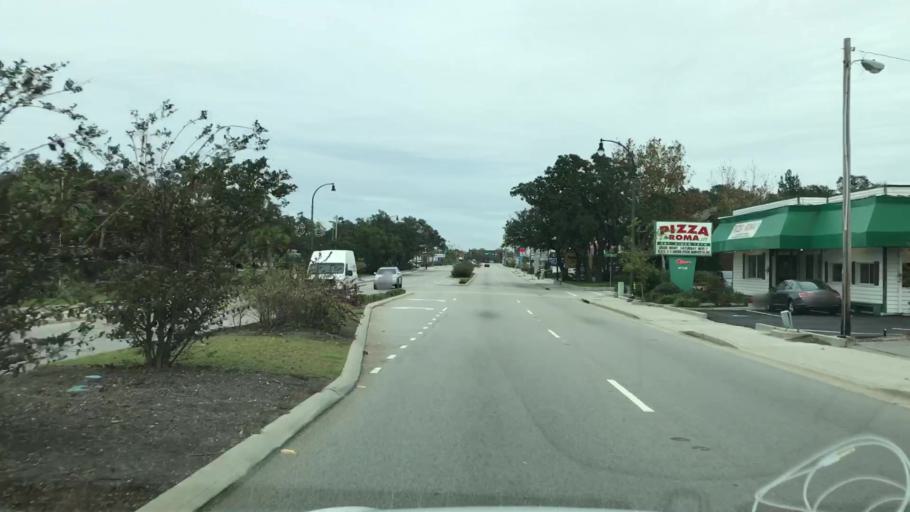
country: US
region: South Carolina
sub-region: Horry County
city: Myrtle Beach
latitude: 33.6894
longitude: -78.8872
